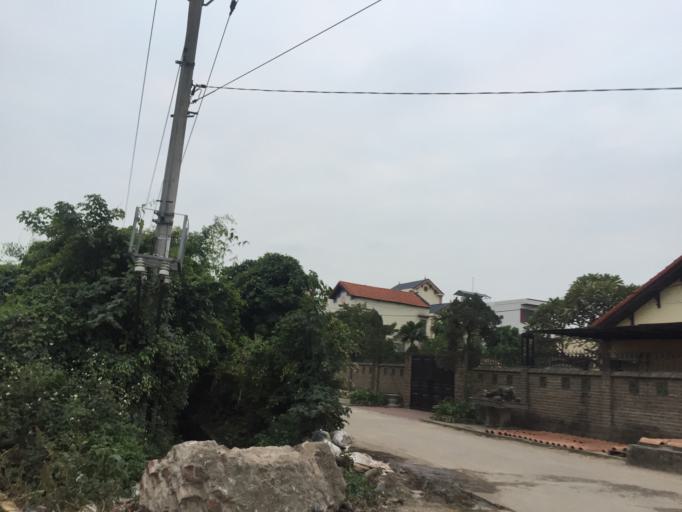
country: VN
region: Hung Yen
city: Van Giang
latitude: 20.9694
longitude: 105.9124
